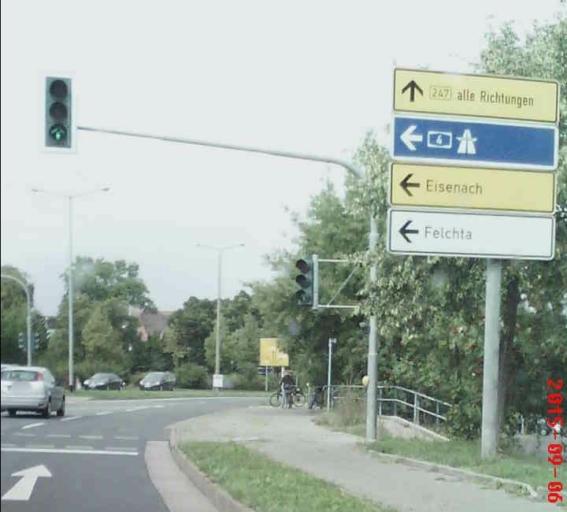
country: DE
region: Thuringia
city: Muehlhausen
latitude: 51.2028
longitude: 10.4675
